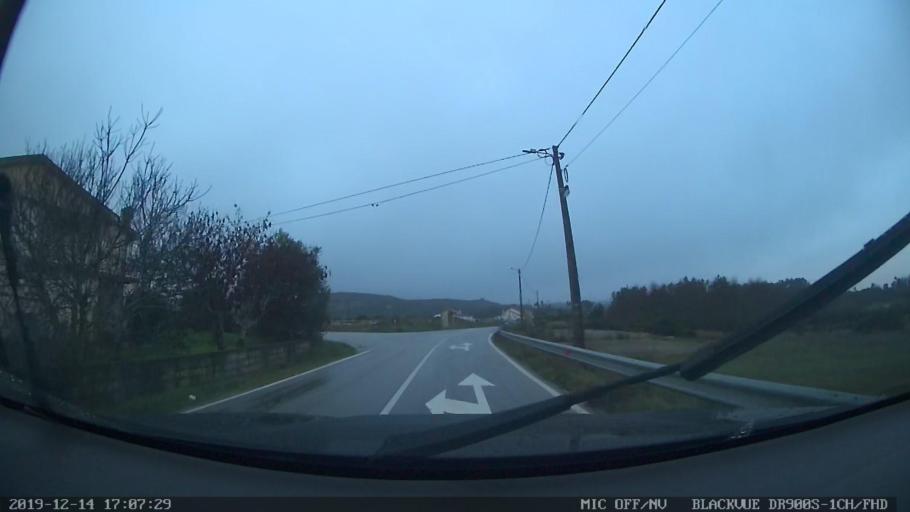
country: PT
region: Vila Real
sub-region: Vila Pouca de Aguiar
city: Vila Pouca de Aguiar
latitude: 41.4621
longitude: -7.5985
